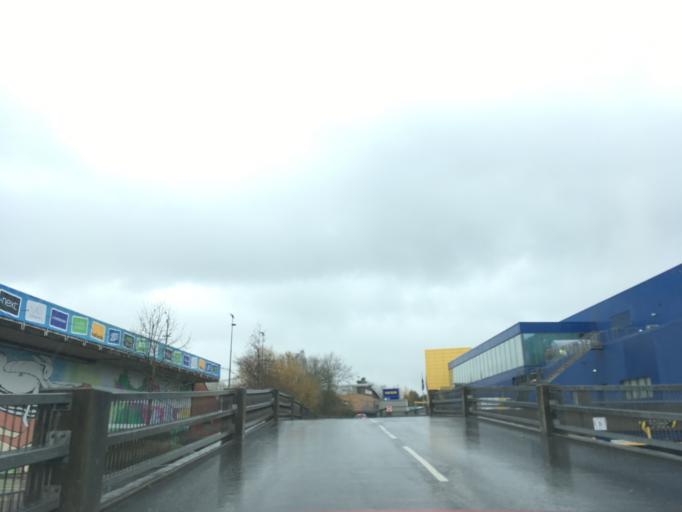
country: GB
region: England
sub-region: Bristol
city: Bristol
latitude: 51.4720
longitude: -2.5664
